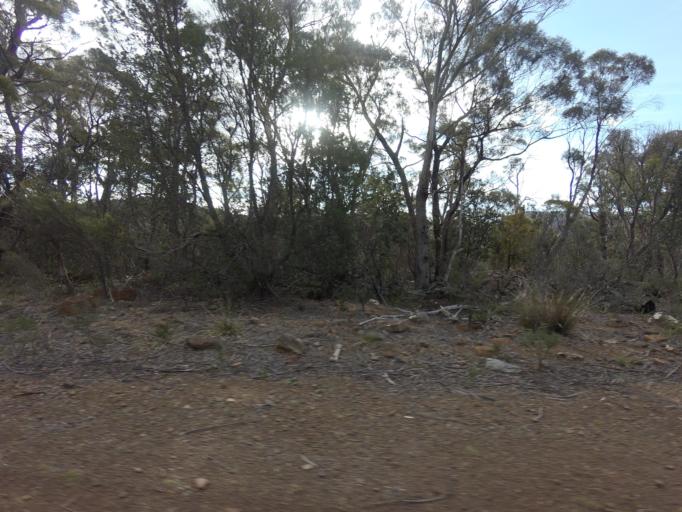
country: AU
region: Tasmania
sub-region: Break O'Day
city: St Helens
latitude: -41.8607
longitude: 148.0236
